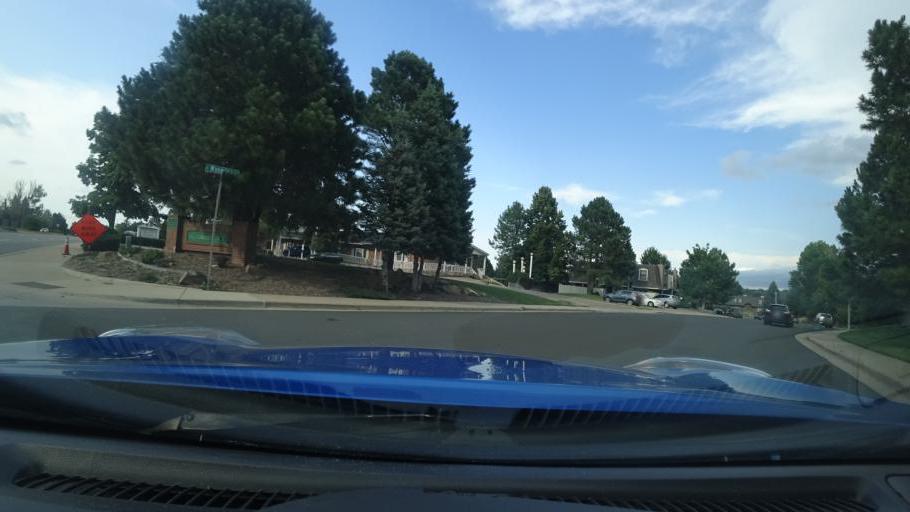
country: US
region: Colorado
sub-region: Adams County
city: Aurora
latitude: 39.6912
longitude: -104.8097
